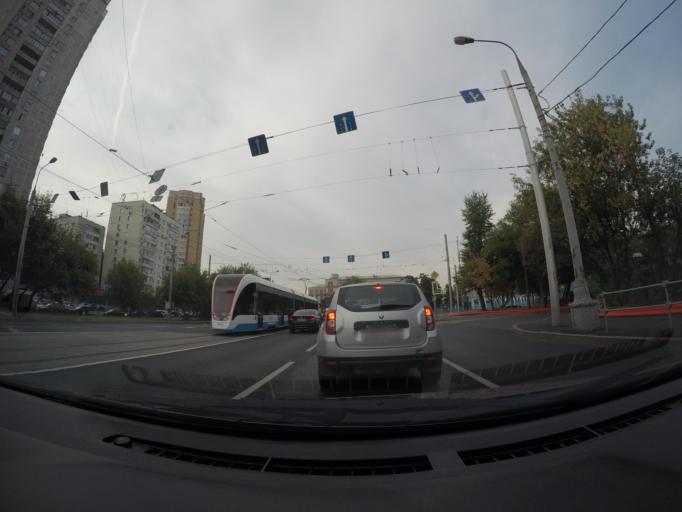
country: RU
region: Moscow
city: Lefortovo
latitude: 55.7792
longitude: 37.7205
